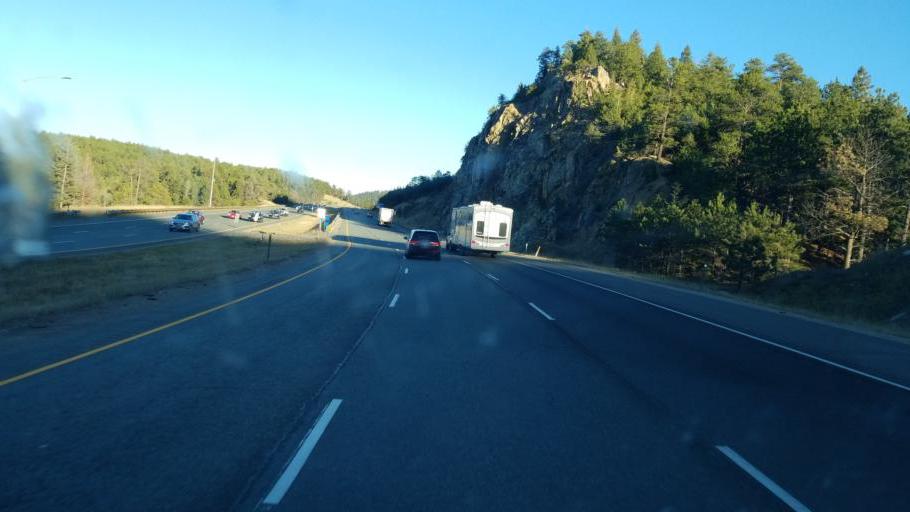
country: US
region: Colorado
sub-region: Jefferson County
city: Kittredge
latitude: 39.7124
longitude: -105.3649
